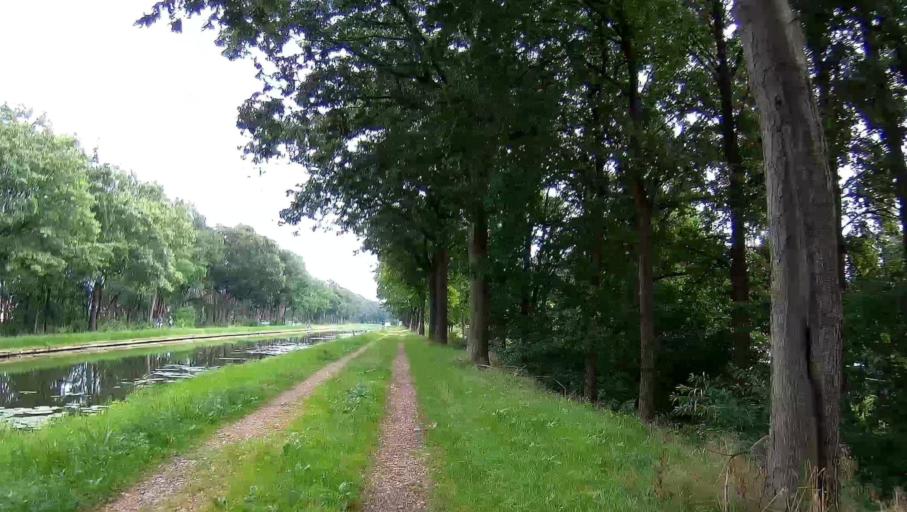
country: BE
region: Flanders
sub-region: Provincie Limburg
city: Leopoldsburg
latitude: 51.1865
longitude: 5.2558
